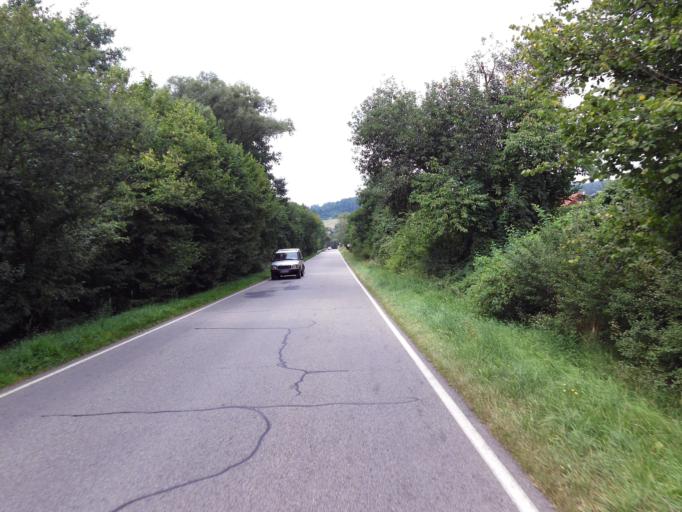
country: CZ
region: Central Bohemia
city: Kamenice
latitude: 49.8705
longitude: 14.5981
